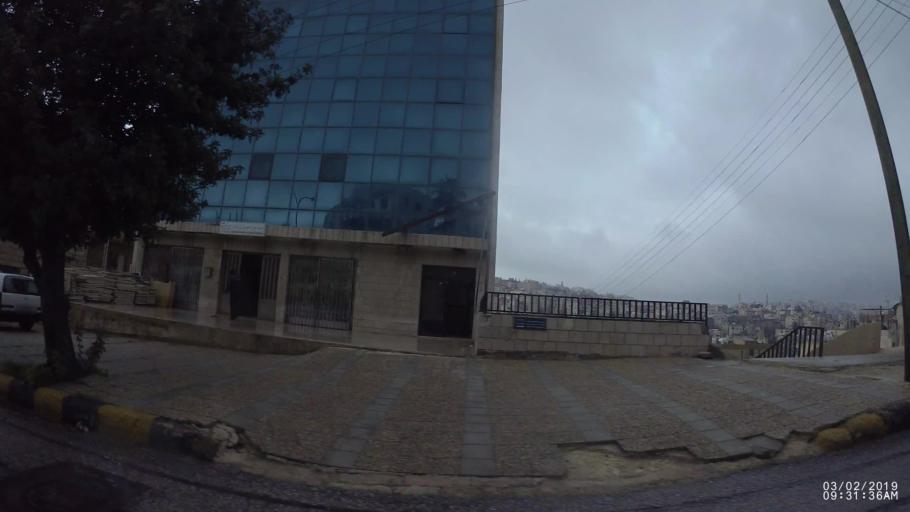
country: JO
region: Amman
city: Amman
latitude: 31.9487
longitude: 35.9102
